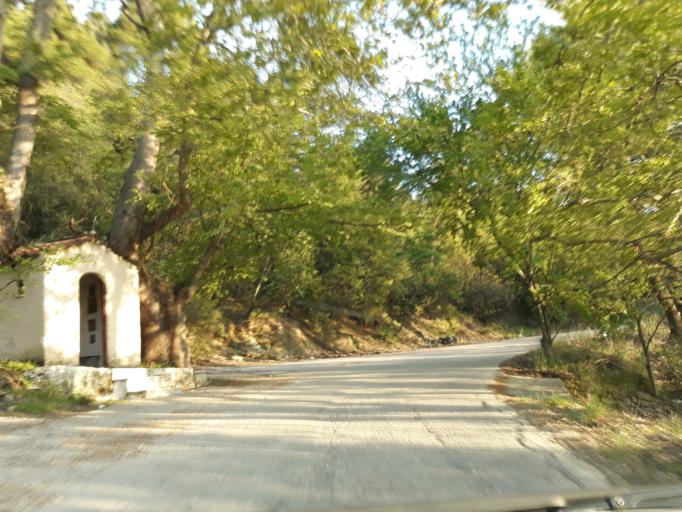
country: GR
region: Attica
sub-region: Nomarchia Anatolikis Attikis
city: Afidnes
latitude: 38.2195
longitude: 23.7798
